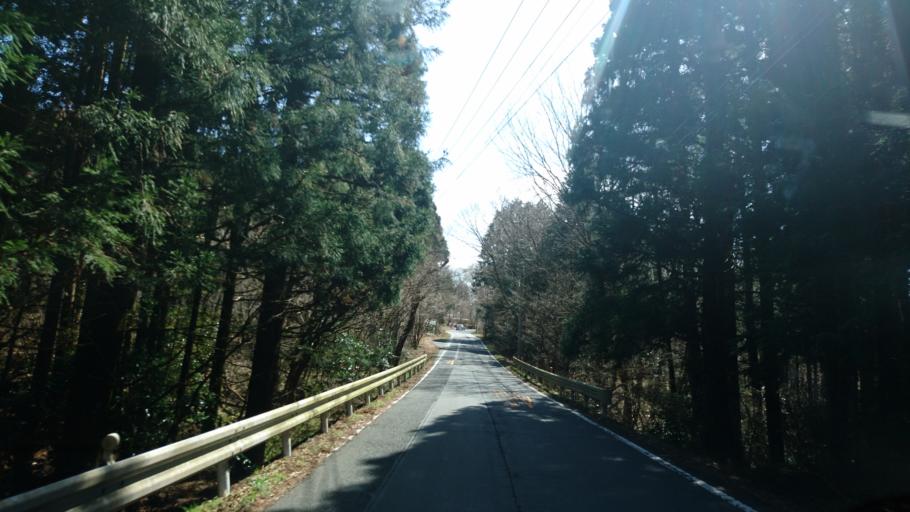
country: JP
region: Shizuoka
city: Fujinomiya
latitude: 35.3562
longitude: 138.5708
